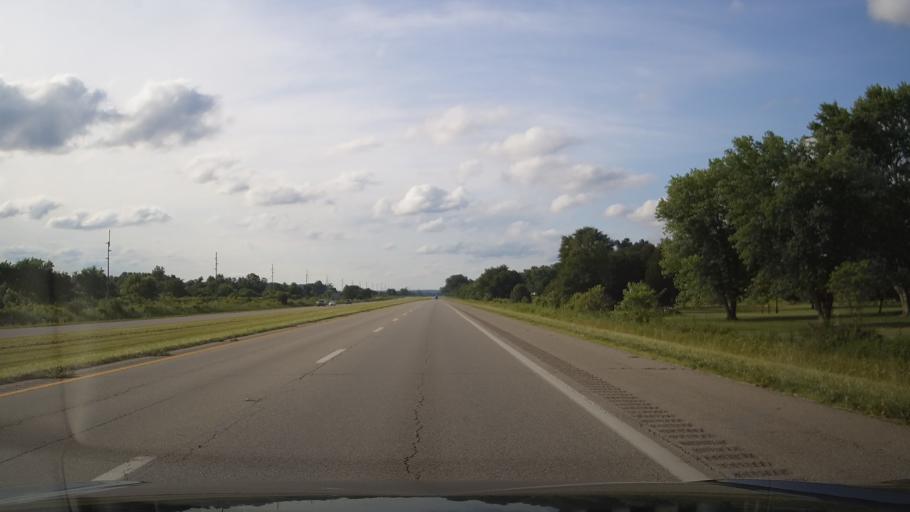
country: US
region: Ohio
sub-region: Scioto County
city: Franklin Furnace
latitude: 38.6646
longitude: -82.8550
